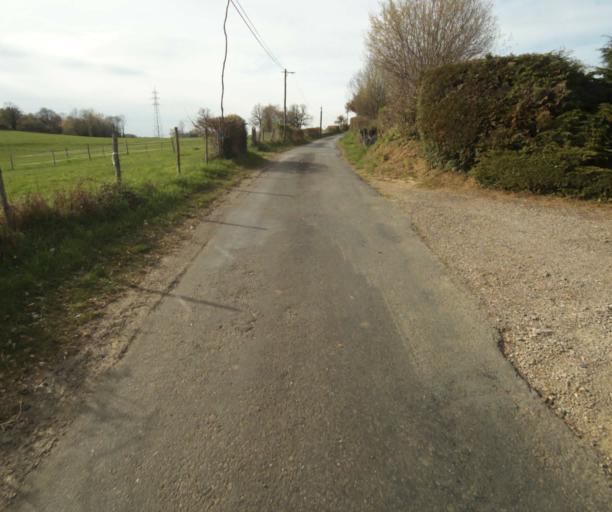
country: FR
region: Limousin
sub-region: Departement de la Correze
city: Naves
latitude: 45.3221
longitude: 1.7430
